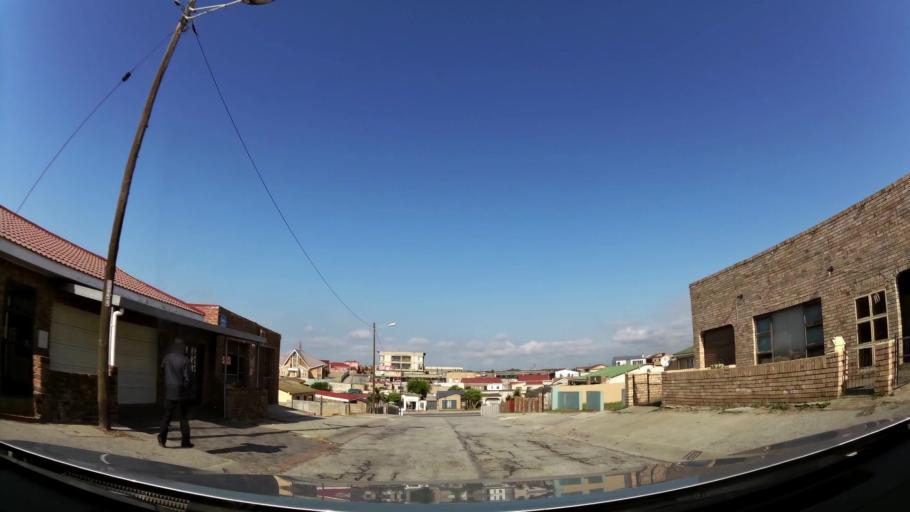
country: ZA
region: Eastern Cape
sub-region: Nelson Mandela Bay Metropolitan Municipality
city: Port Elizabeth
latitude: -33.9233
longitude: 25.5349
